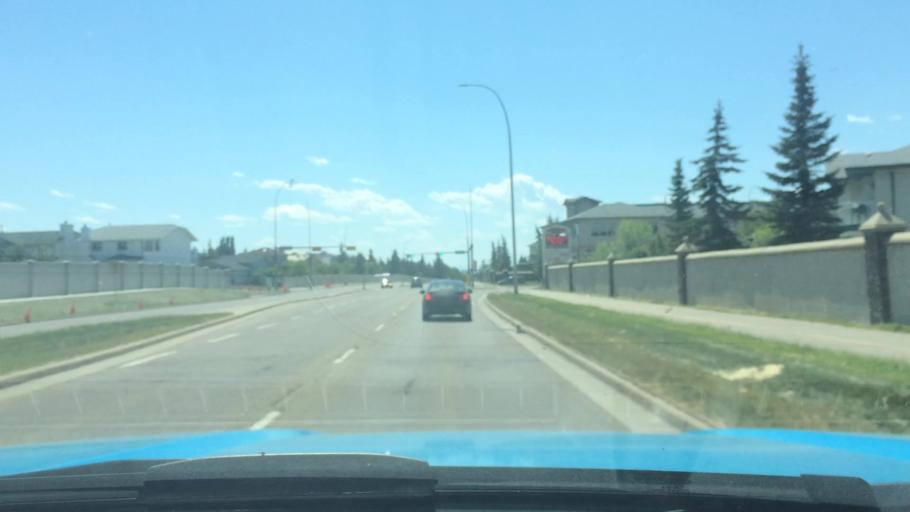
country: CA
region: Alberta
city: Calgary
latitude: 51.1387
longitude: -114.1844
